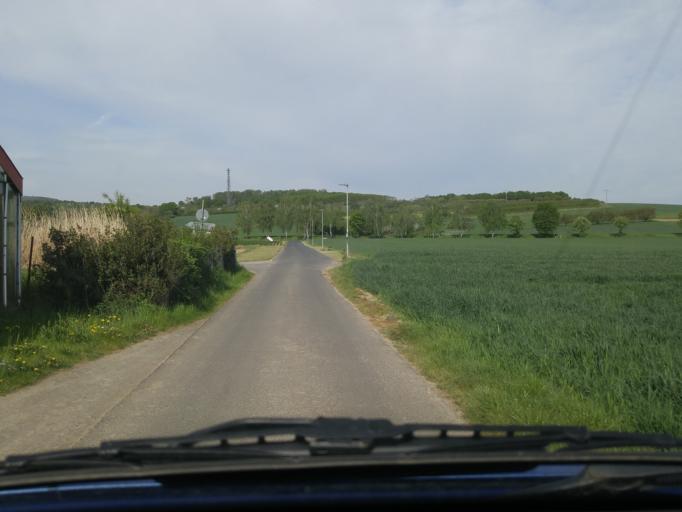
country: DE
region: Hesse
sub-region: Regierungsbezirk Darmstadt
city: Bad Nauheim
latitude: 50.3434
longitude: 8.7321
